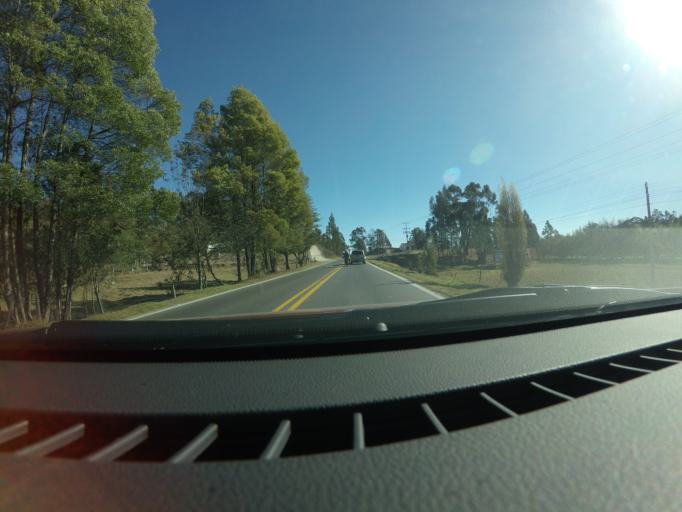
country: CO
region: Cundinamarca
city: Sutatausa
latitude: 5.2677
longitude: -73.8418
